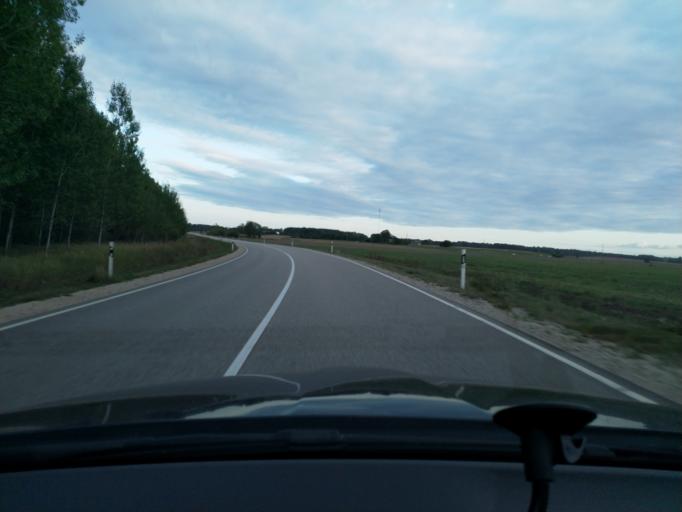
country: LV
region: Kandava
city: Kandava
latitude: 56.9348
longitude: 22.7386
